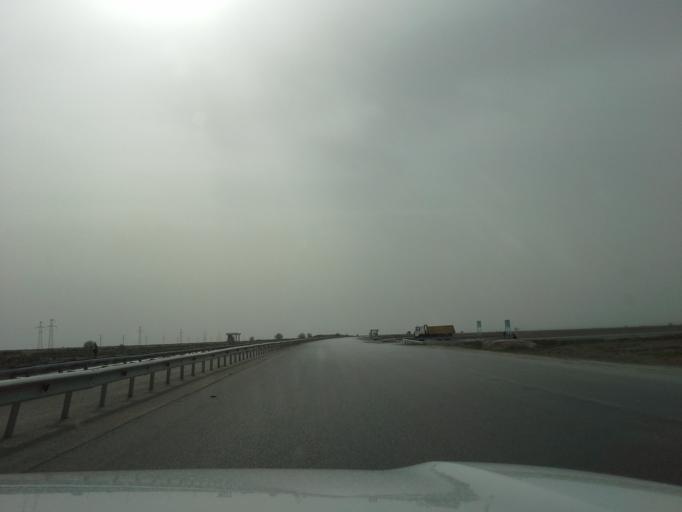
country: TM
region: Ahal
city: Kaka
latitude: 37.4751
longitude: 59.4928
